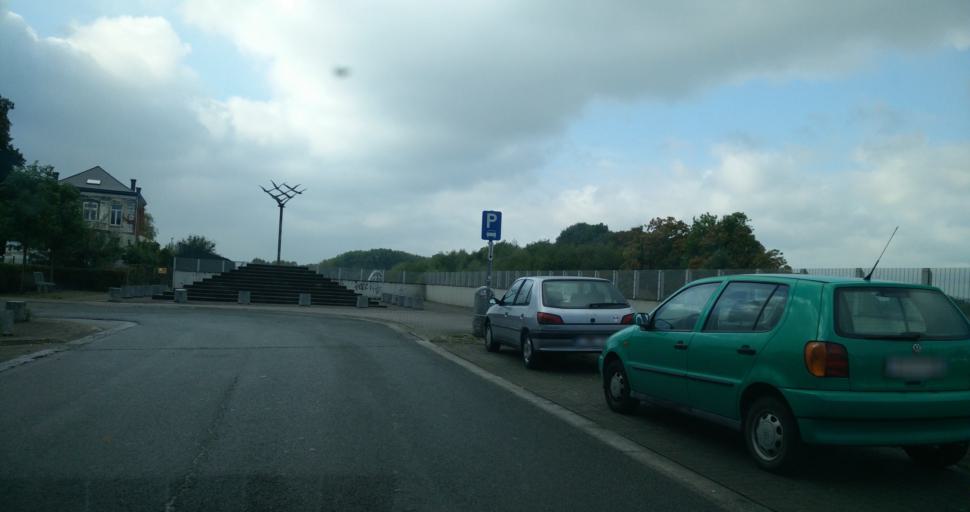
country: BE
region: Flanders
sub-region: Provincie Vlaams-Brabant
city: Halle
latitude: 50.7309
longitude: 4.2374
